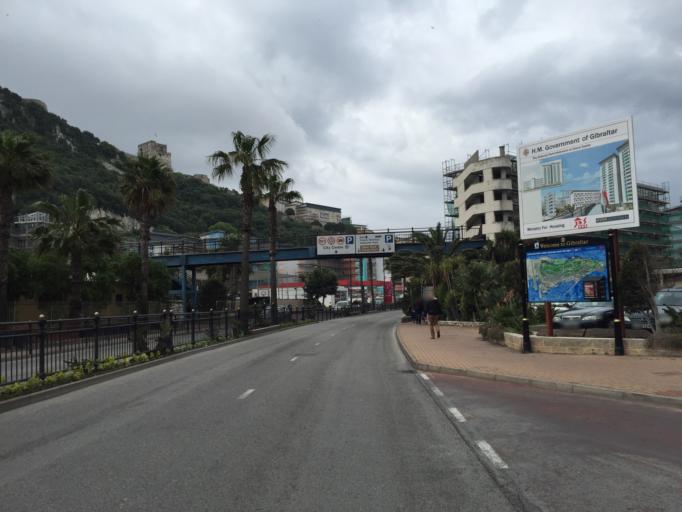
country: GI
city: Gibraltar
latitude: 36.1478
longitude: -5.3497
